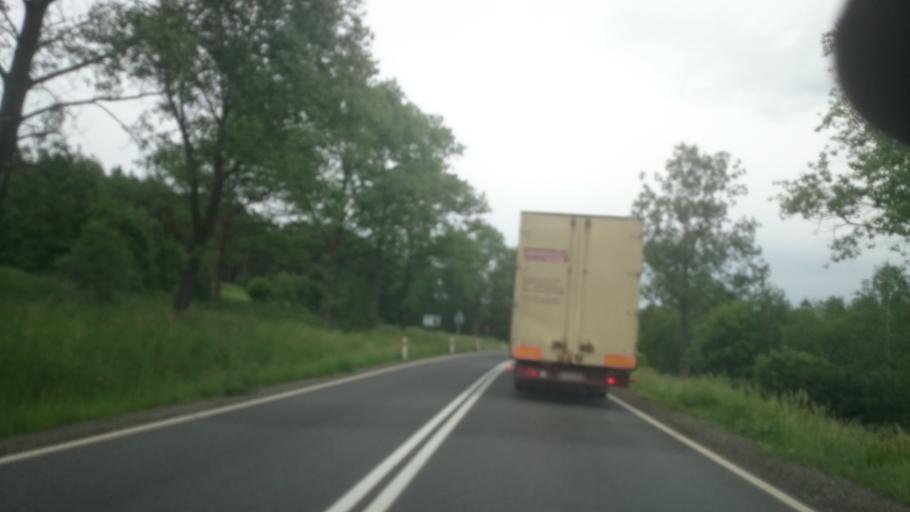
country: PL
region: Lower Silesian Voivodeship
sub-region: Powiat klodzki
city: Klodzko
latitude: 50.4341
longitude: 16.7078
